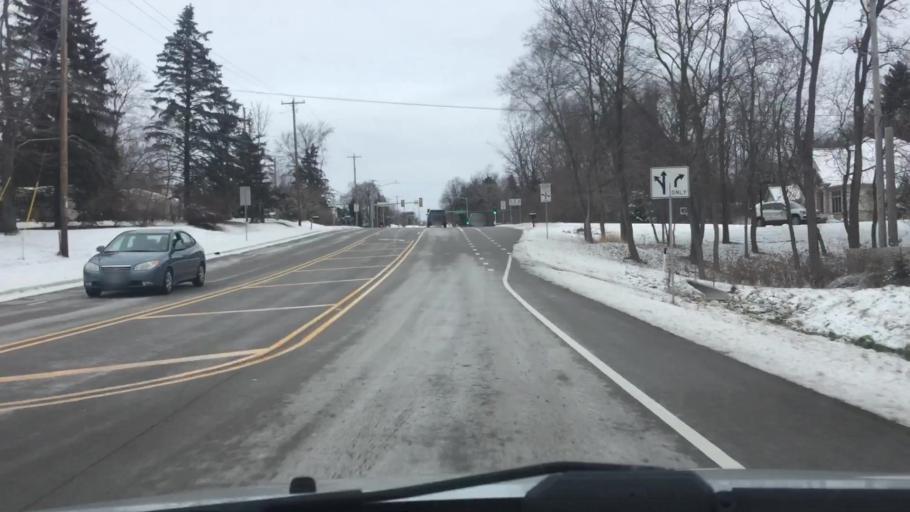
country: US
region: Wisconsin
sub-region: Waukesha County
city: Brookfield
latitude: 43.0734
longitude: -88.1059
